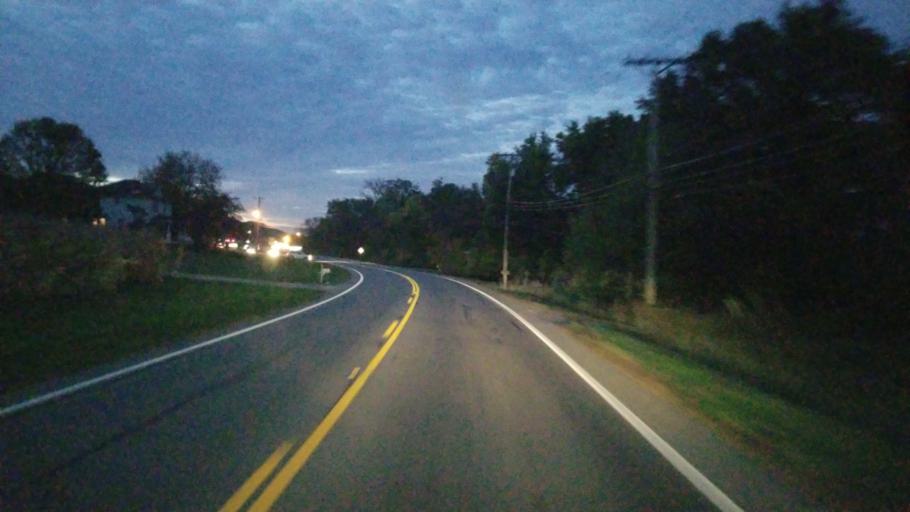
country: US
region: Ohio
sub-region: Scioto County
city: Lucasville
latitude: 38.8765
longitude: -83.0162
